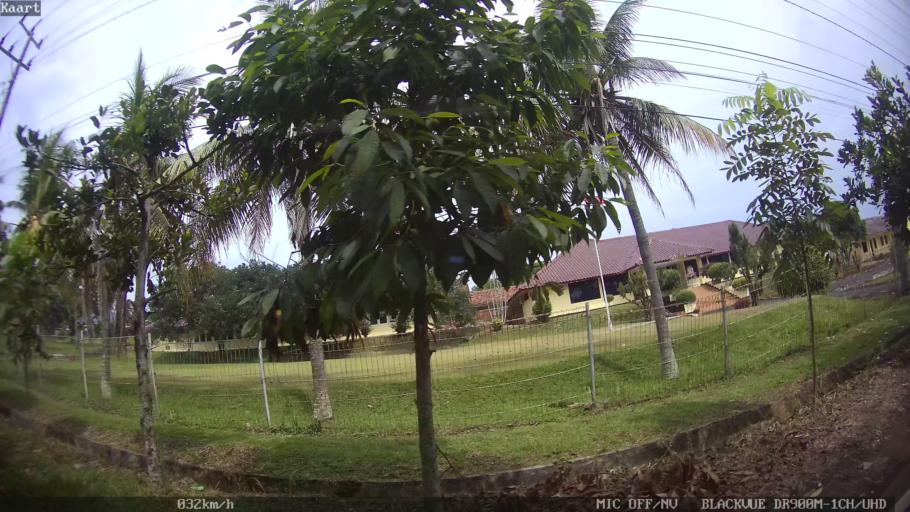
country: ID
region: Lampung
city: Bandarlampung
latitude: -5.4040
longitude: 105.2006
